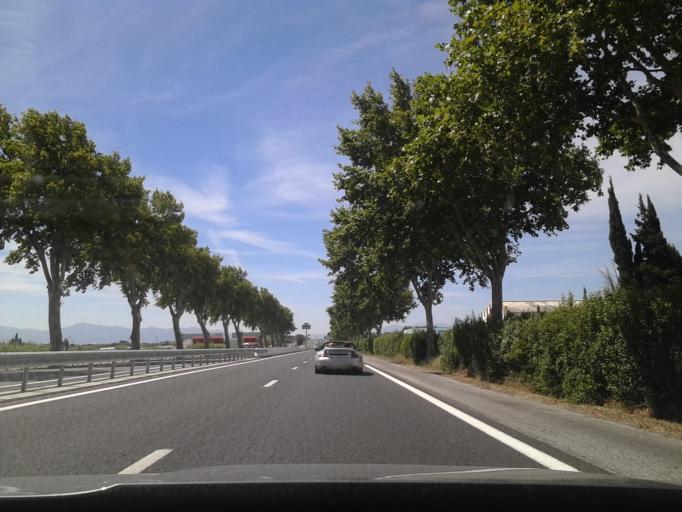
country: FR
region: Languedoc-Roussillon
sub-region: Departement des Pyrenees-Orientales
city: Pia
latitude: 42.7606
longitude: 2.8976
